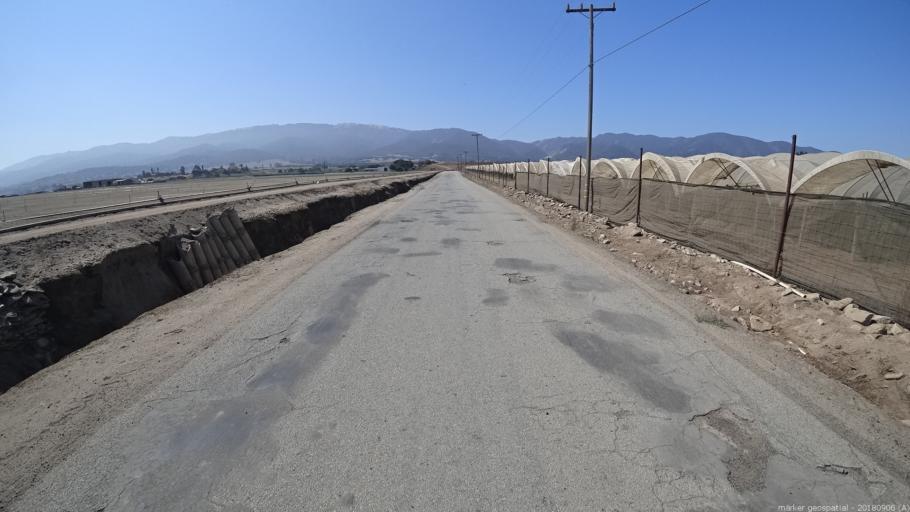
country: US
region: California
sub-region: Monterey County
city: Chualar
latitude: 36.5922
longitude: -121.6037
